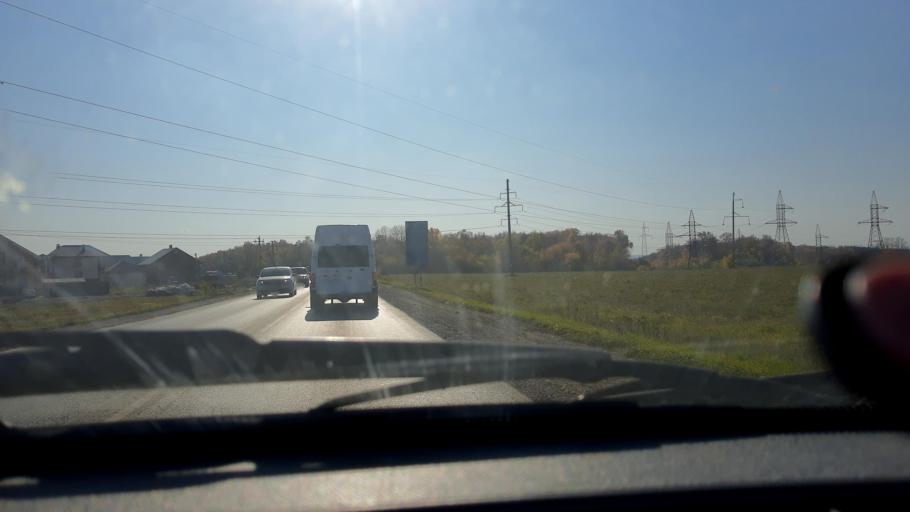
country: RU
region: Bashkortostan
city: Mikhaylovka
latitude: 54.8288
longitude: 55.8850
